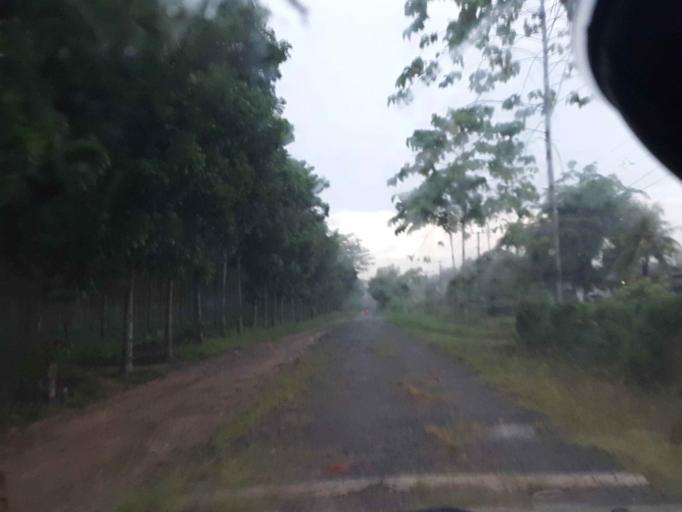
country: ID
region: Lampung
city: Kedaton
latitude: -5.3623
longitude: 105.3632
